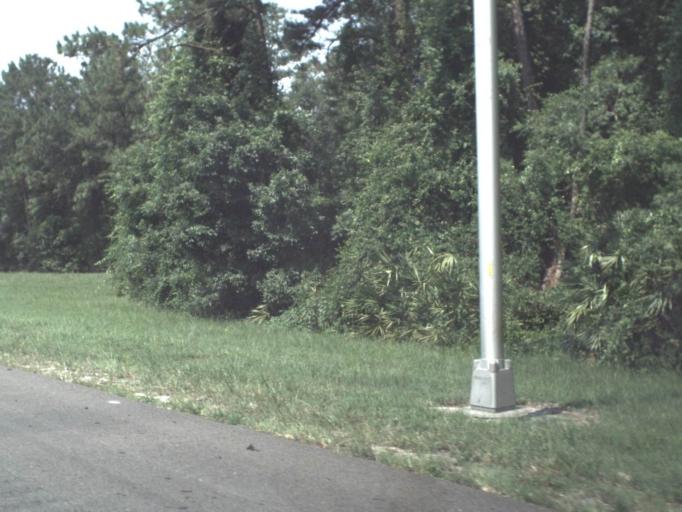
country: US
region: Florida
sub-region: Duval County
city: Jacksonville
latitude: 30.4560
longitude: -81.6506
